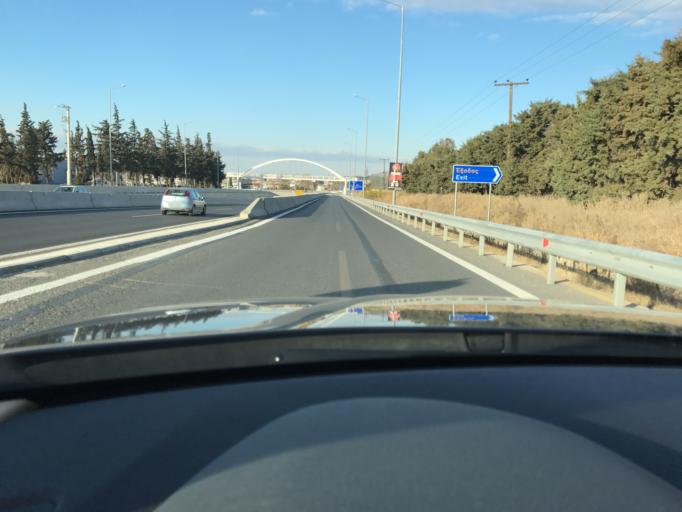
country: GR
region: Central Macedonia
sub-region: Nomos Thessalonikis
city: Efkarpia
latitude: 40.6800
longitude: 22.9503
